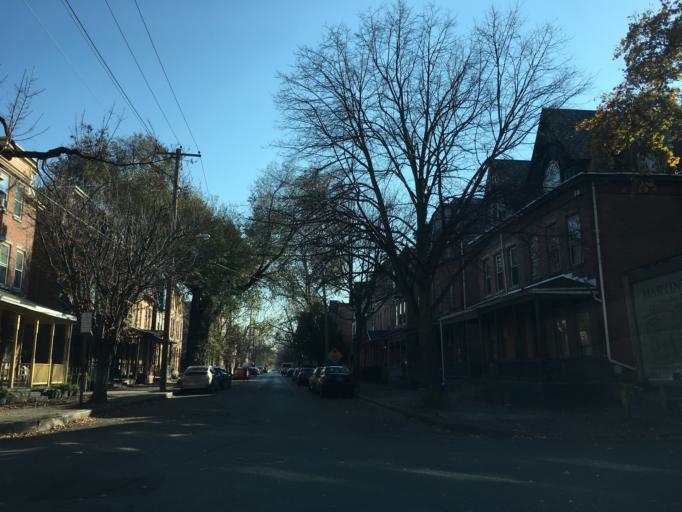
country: US
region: Pennsylvania
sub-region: Dauphin County
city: Harrisburg
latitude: 40.2736
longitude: -76.8934
